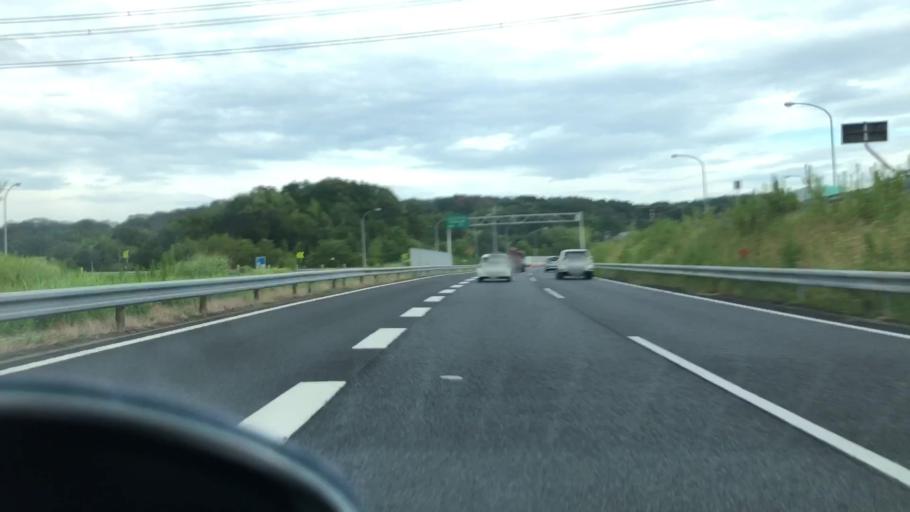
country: JP
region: Hyogo
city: Sandacho
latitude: 34.8935
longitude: 135.1517
